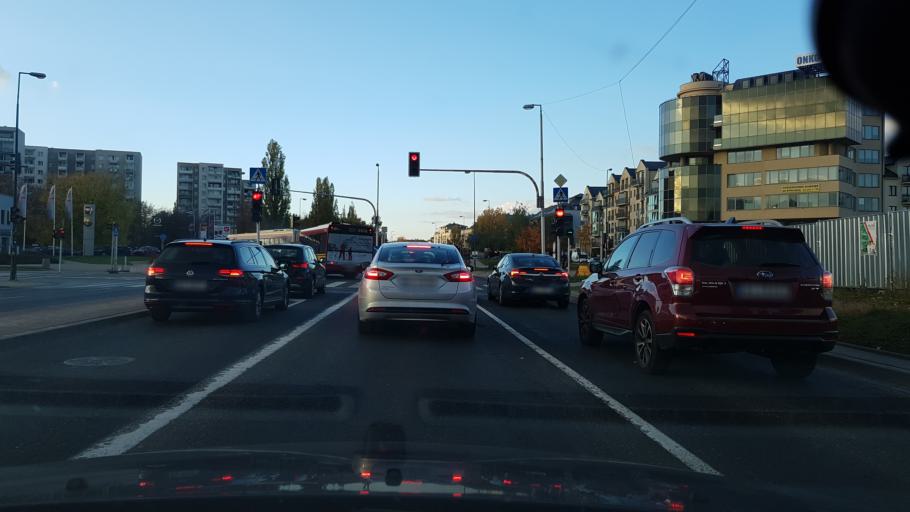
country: PL
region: Masovian Voivodeship
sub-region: Warszawa
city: Ursynow
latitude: 52.1491
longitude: 21.0601
